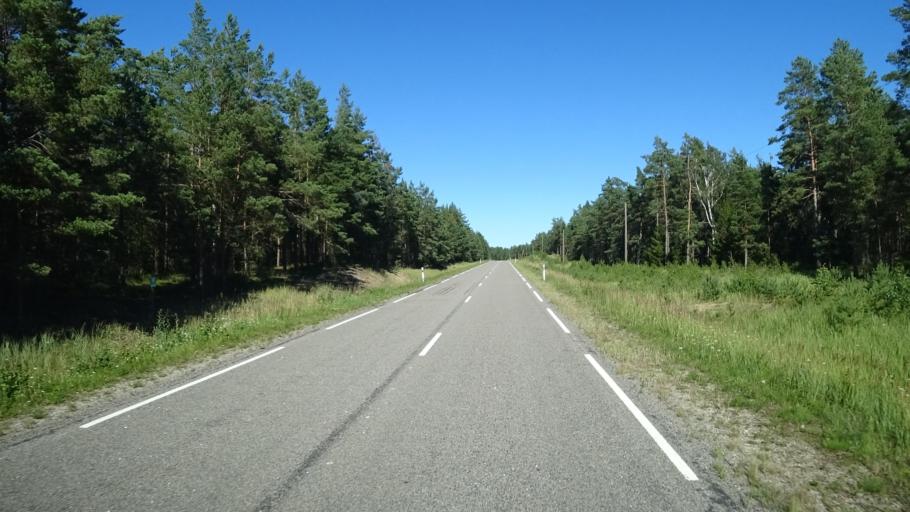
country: LV
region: Dundaga
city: Dundaga
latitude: 57.6800
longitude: 22.3534
